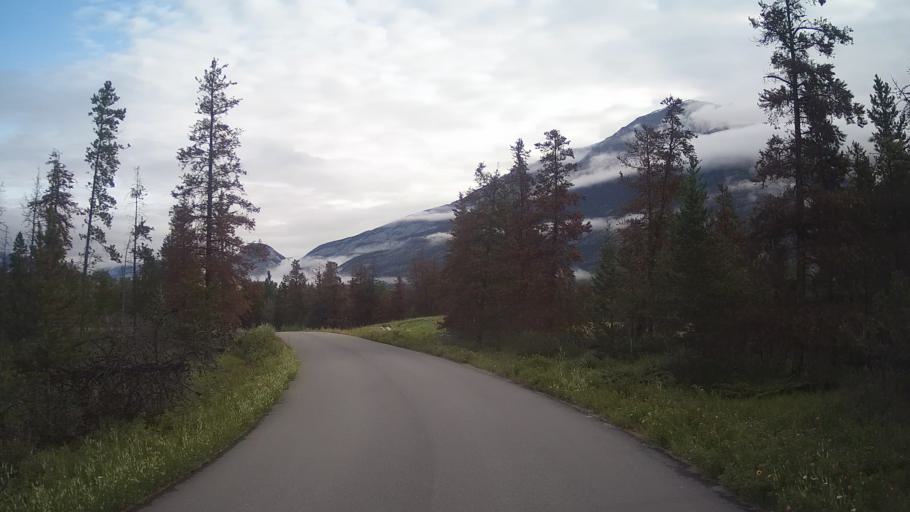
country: CA
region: Alberta
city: Jasper Park Lodge
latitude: 52.9682
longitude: -118.0589
